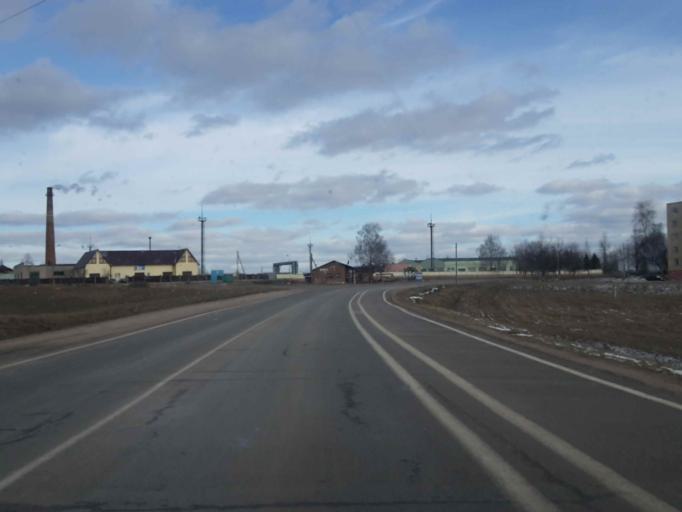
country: BY
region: Minsk
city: Myadzyel
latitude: 54.8857
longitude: 26.9337
